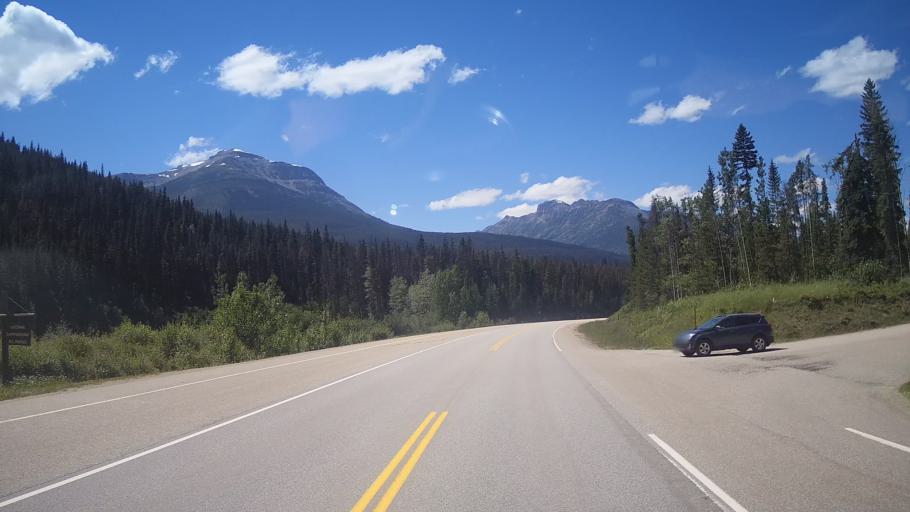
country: CA
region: Alberta
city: Jasper Park Lodge
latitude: 52.8489
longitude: -118.5715
